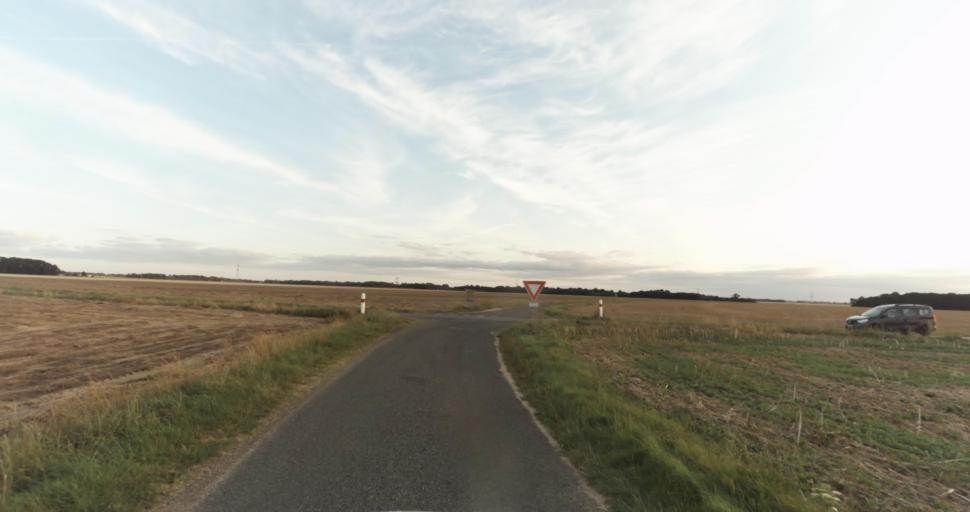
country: FR
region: Haute-Normandie
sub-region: Departement de l'Eure
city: La Madeleine-de-Nonancourt
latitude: 48.8679
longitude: 1.2305
